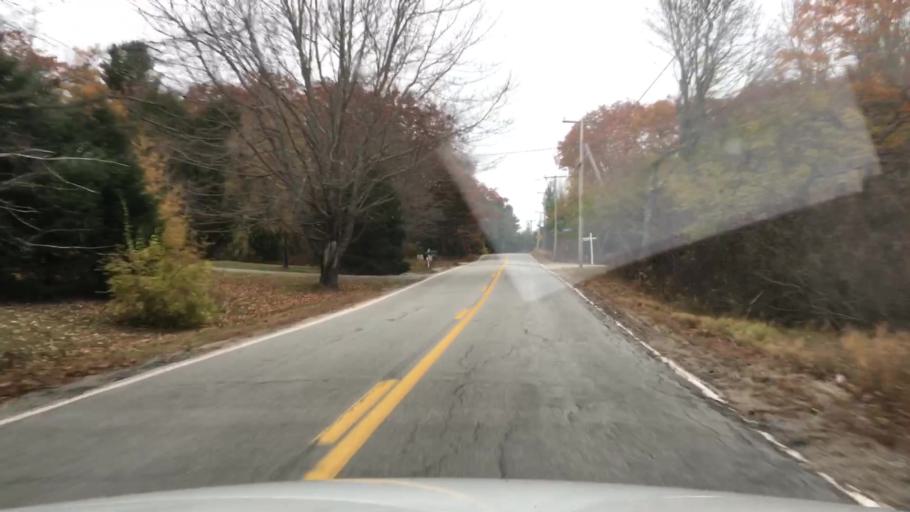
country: US
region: Maine
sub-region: Hancock County
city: Sedgwick
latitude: 44.3310
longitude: -68.5682
